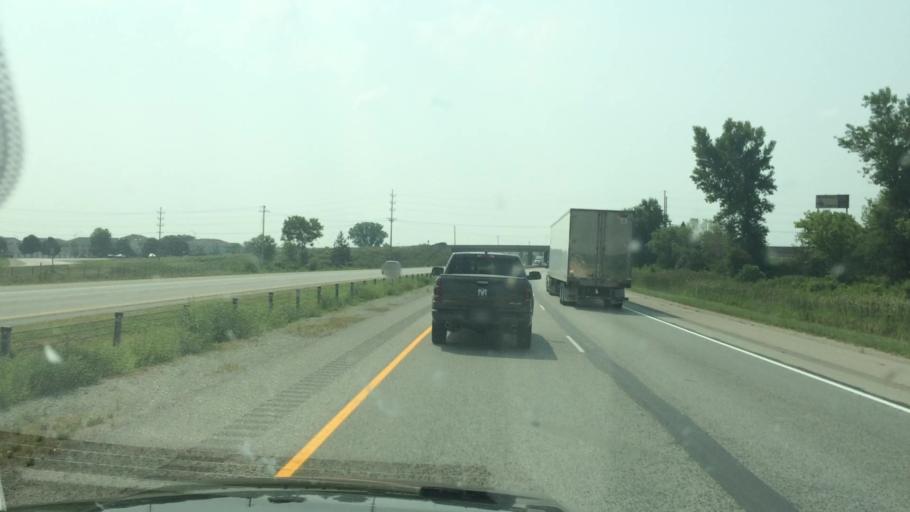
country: US
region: Wisconsin
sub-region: Fond du Lac County
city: North Fond du Lac
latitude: 43.7940
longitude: -88.4842
